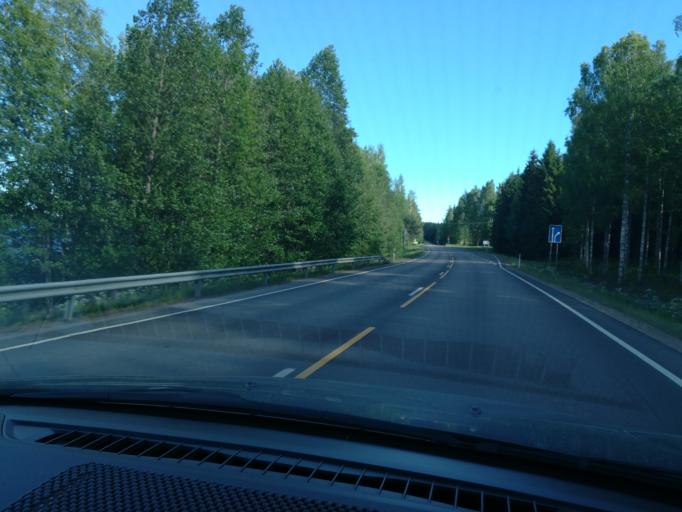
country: FI
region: Southern Savonia
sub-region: Mikkeli
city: Puumala
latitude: 61.5122
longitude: 28.1787
